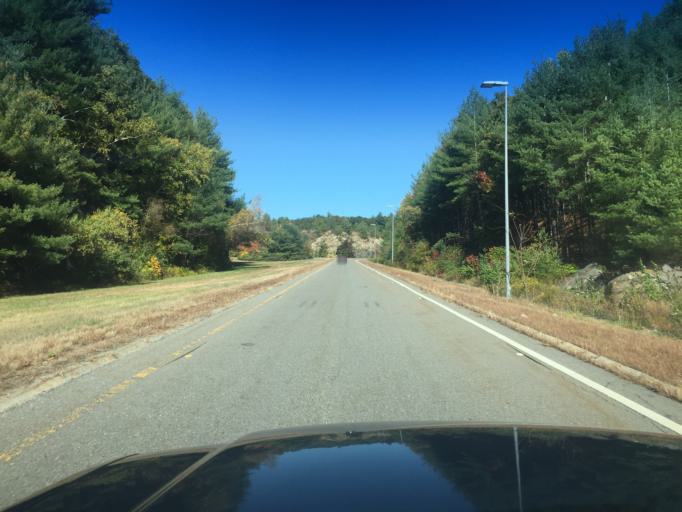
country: US
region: Massachusetts
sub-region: Middlesex County
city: Hudson
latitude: 42.3614
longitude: -71.5869
